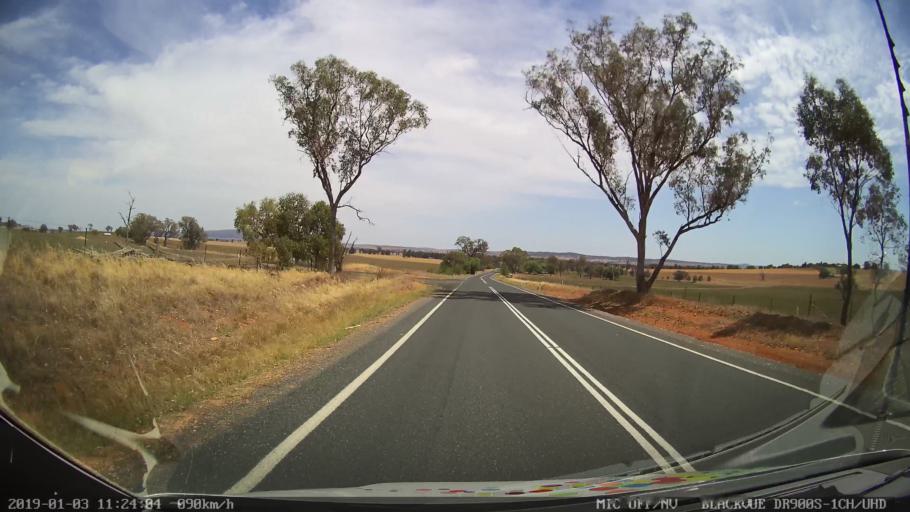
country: AU
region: New South Wales
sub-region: Weddin
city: Grenfell
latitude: -34.0561
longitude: 148.2378
